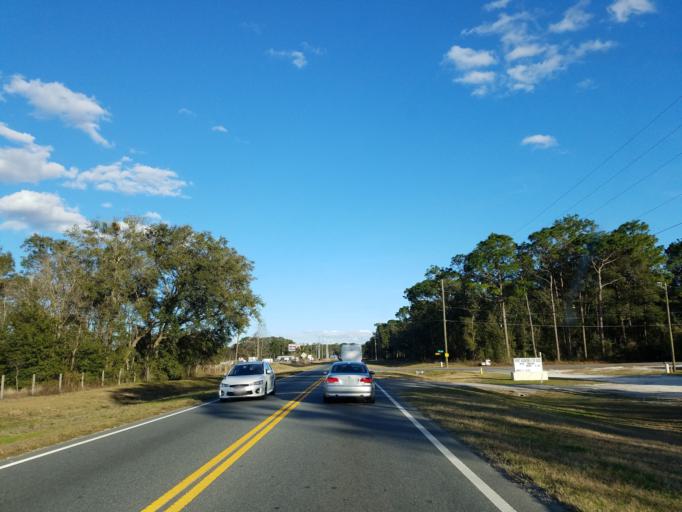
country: US
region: Florida
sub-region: Sumter County
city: Lake Panasoffkee
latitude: 28.7489
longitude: -82.0698
